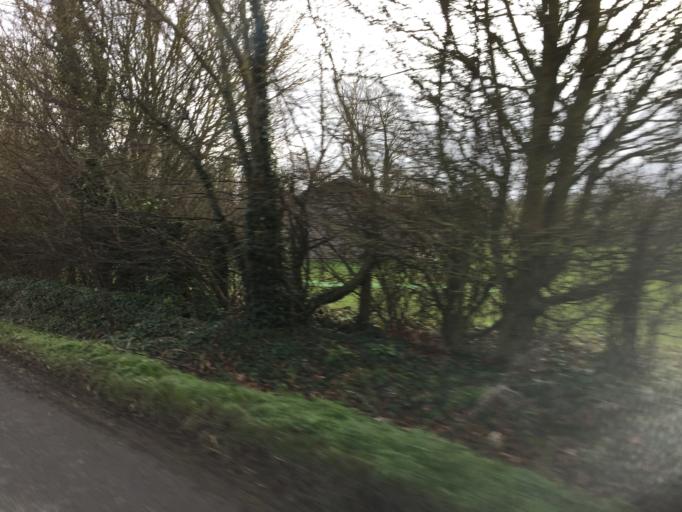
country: GB
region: England
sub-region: Oxfordshire
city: Blewbury
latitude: 51.5678
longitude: -1.2432
